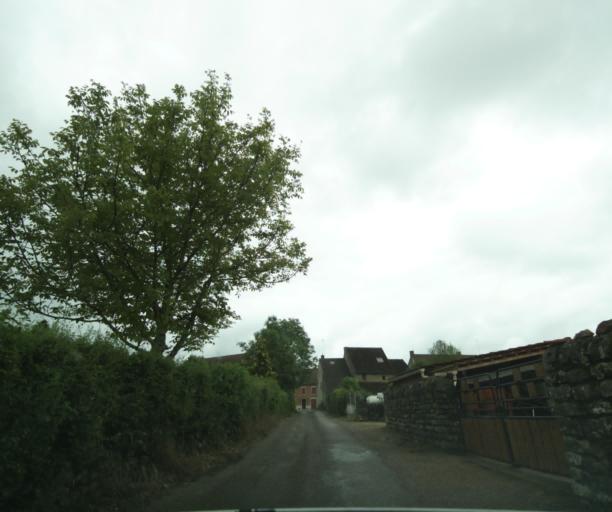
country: FR
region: Bourgogne
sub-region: Departement de Saone-et-Loire
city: Charolles
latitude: 46.4724
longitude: 4.3324
